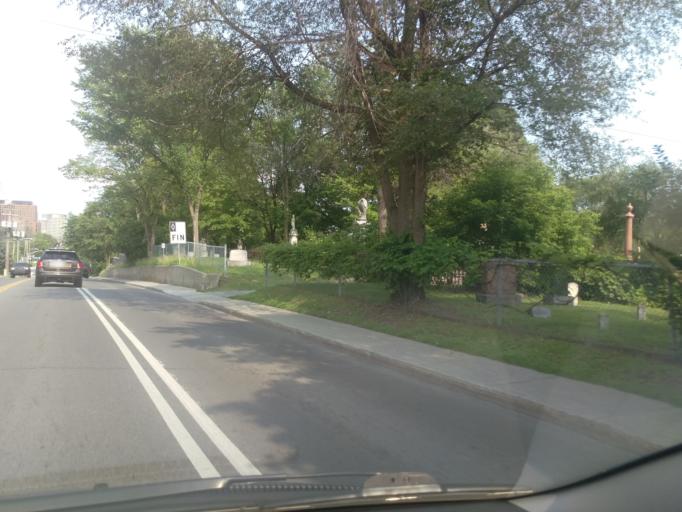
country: CA
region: Ontario
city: Ottawa
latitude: 45.4230
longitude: -75.7370
